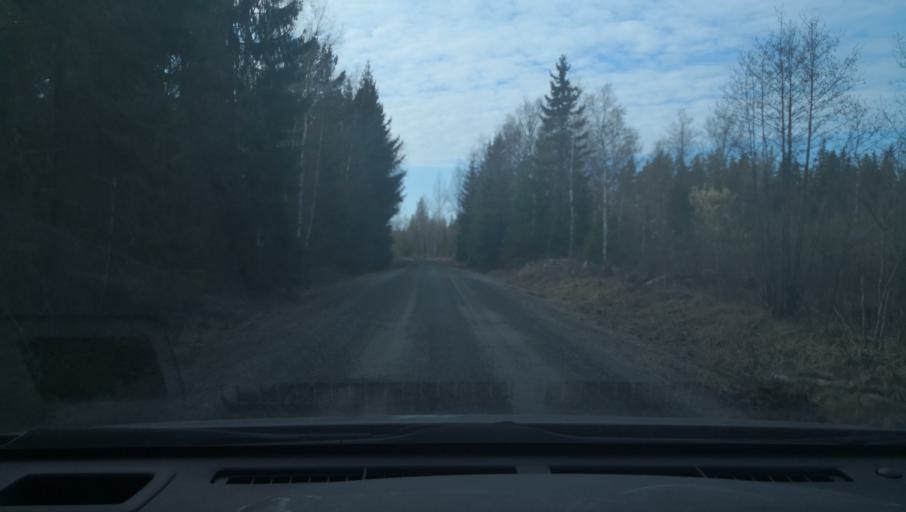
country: SE
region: Uppsala
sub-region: Heby Kommun
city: Heby
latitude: 59.8546
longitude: 16.8675
